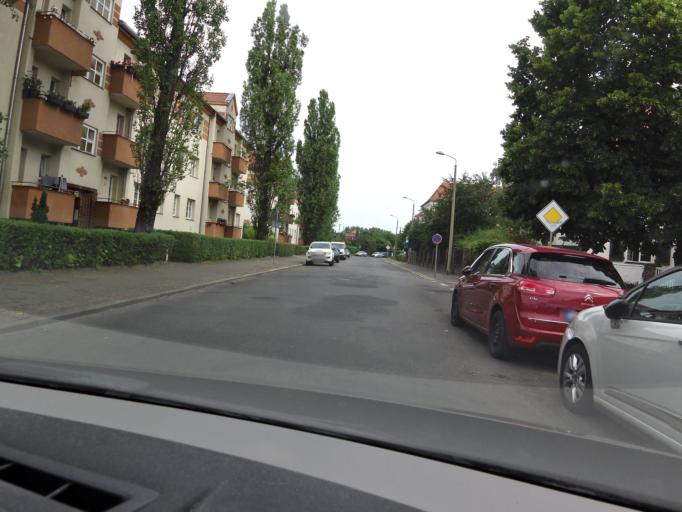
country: DE
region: Saxony
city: Leipzig
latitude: 51.3714
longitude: 12.4051
